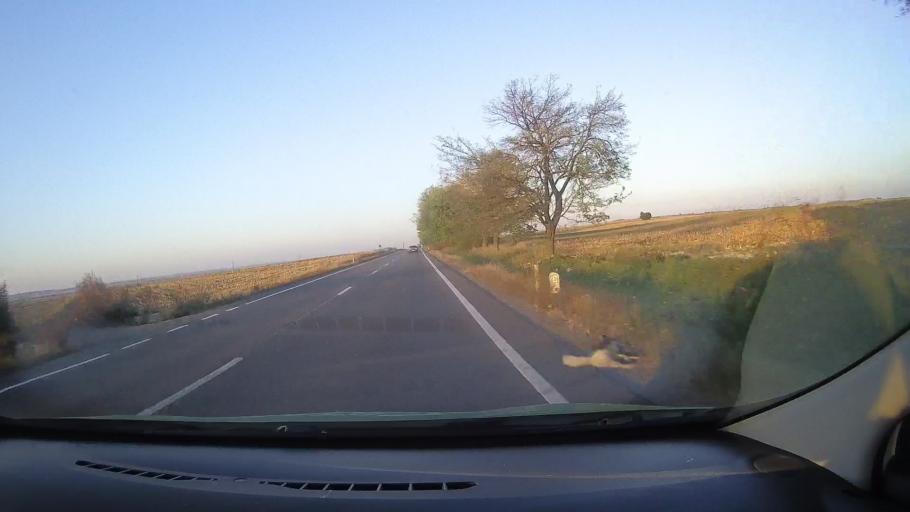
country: RO
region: Bihor
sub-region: Comuna Rosiori
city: Rosiori
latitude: 47.2683
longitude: 21.9736
